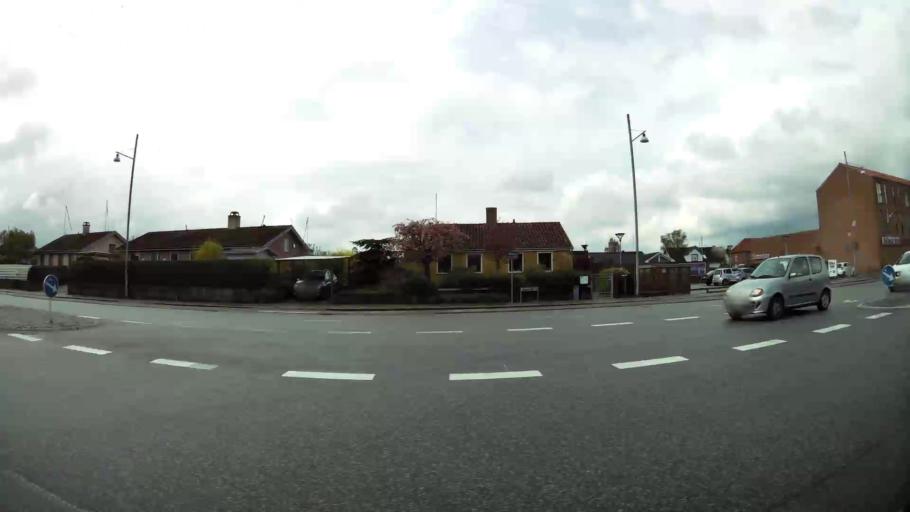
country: DK
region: Capital Region
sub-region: Glostrup Kommune
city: Glostrup
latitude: 55.6610
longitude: 12.4030
